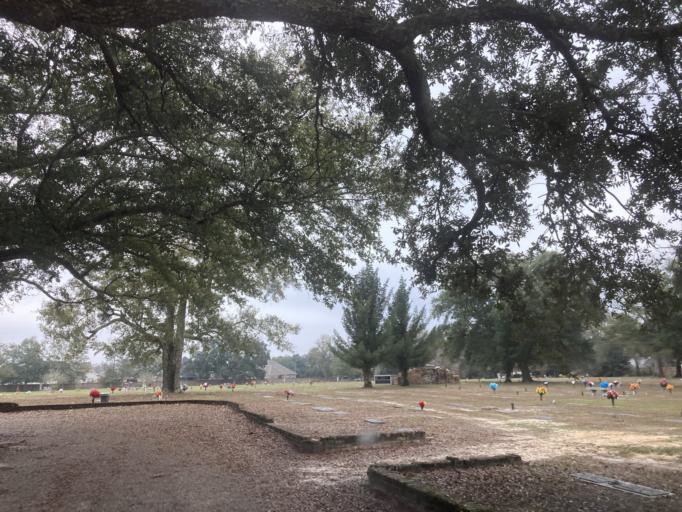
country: US
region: Mississippi
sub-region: Harrison County
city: West Gulfport
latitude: 30.4108
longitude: -89.0302
